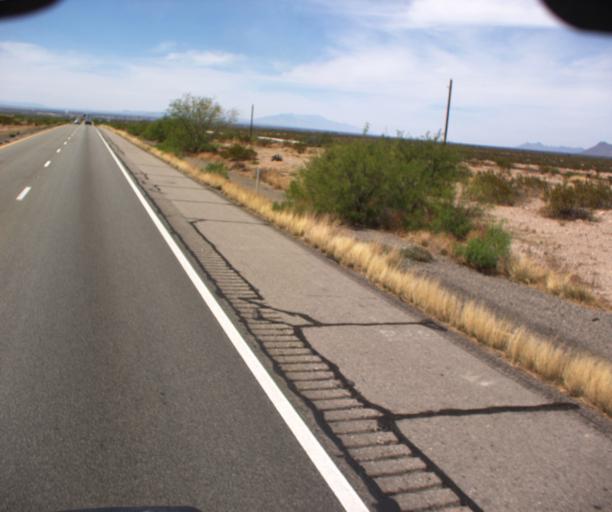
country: US
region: New Mexico
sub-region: Hidalgo County
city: Lordsburg
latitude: 32.2482
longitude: -109.1376
